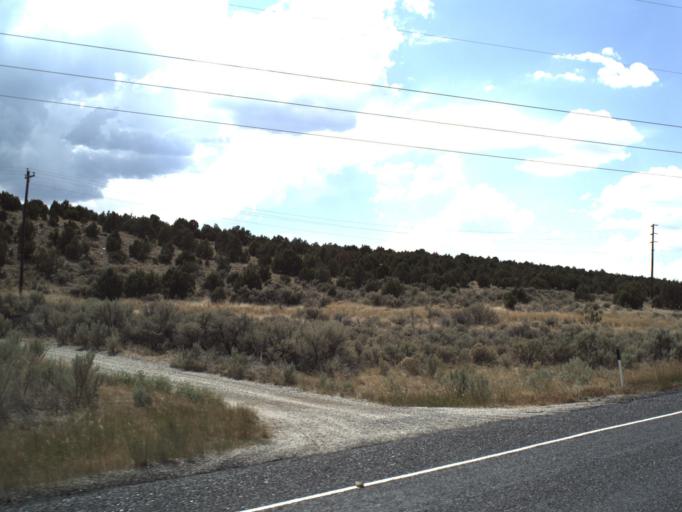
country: US
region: Idaho
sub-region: Minidoka County
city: Rupert
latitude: 41.9740
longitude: -113.1566
